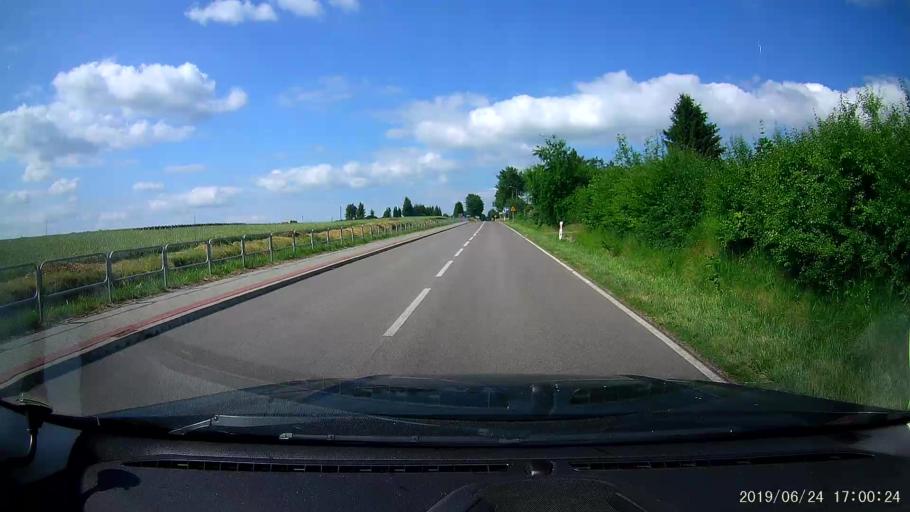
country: PL
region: Lublin Voivodeship
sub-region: Powiat tomaszowski
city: Telatyn
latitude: 50.5260
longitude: 23.9149
